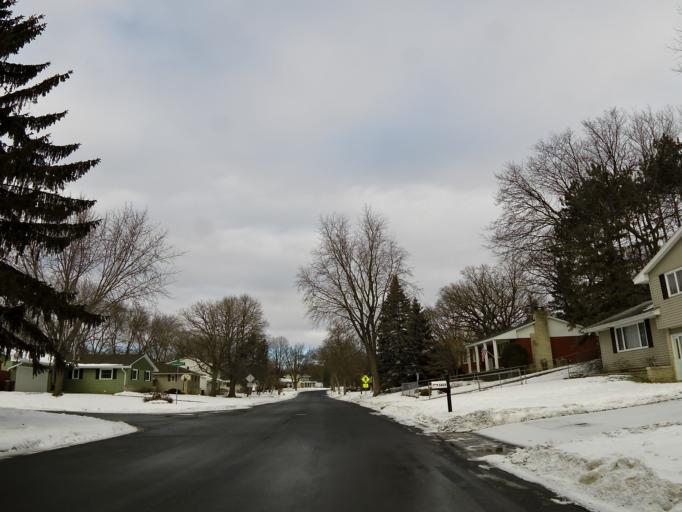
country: US
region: Minnesota
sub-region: Washington County
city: Woodbury
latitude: 44.9281
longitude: -92.9799
